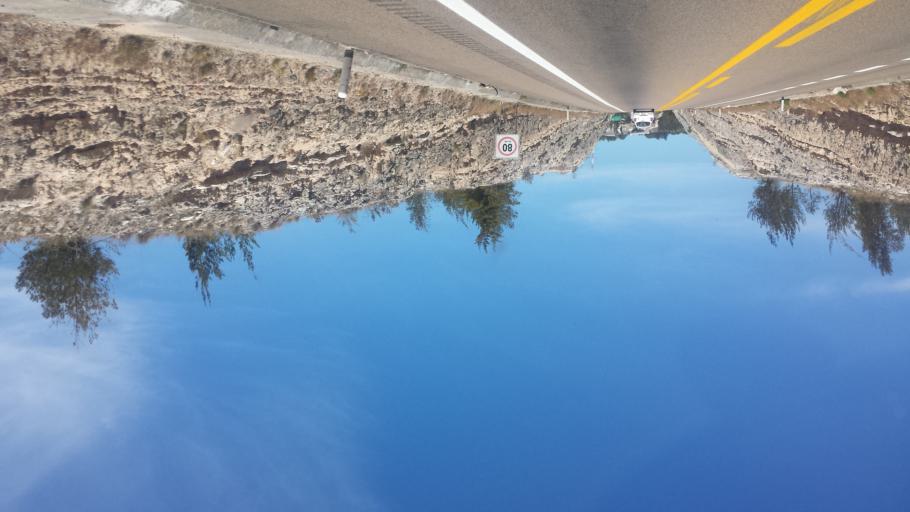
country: MX
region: Oaxaca
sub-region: Villa Tejupam de la Union
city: Villa Tejupam de la Union
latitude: 17.8724
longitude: -97.3755
